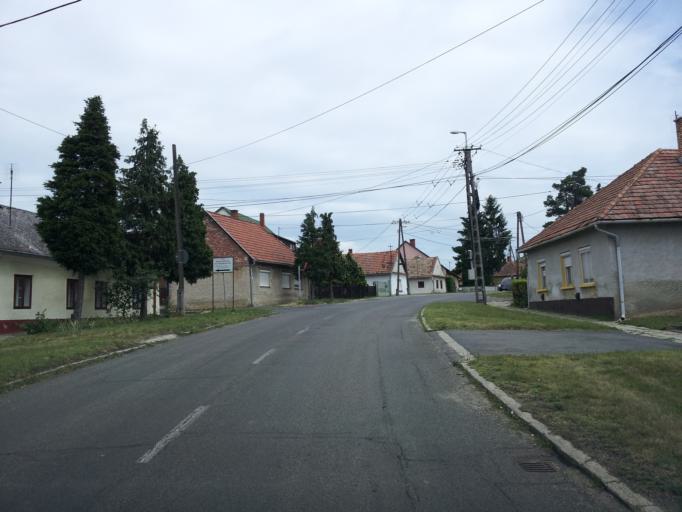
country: HU
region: Vas
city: Vasvar
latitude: 47.0509
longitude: 16.8039
